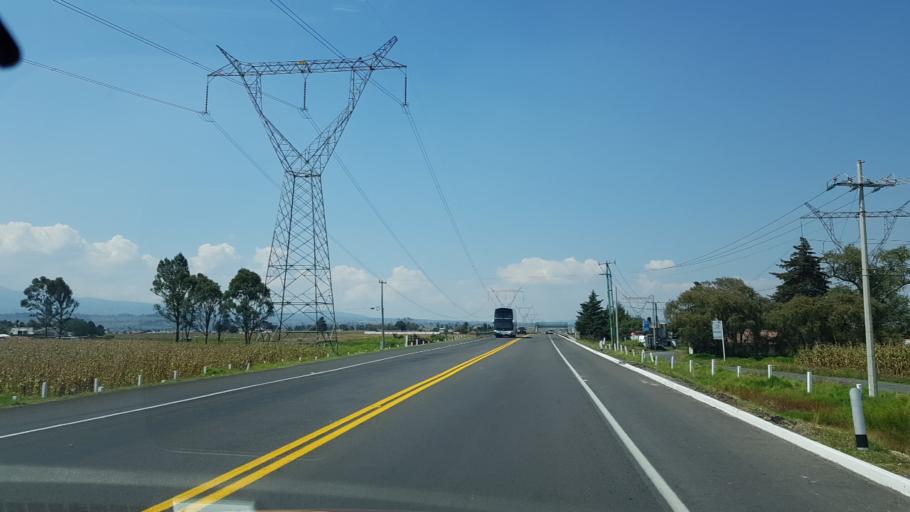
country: MX
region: Mexico
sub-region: Almoloya de Juarez
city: Fraccionamiento Colinas del Sol
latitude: 19.3866
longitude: -99.7451
